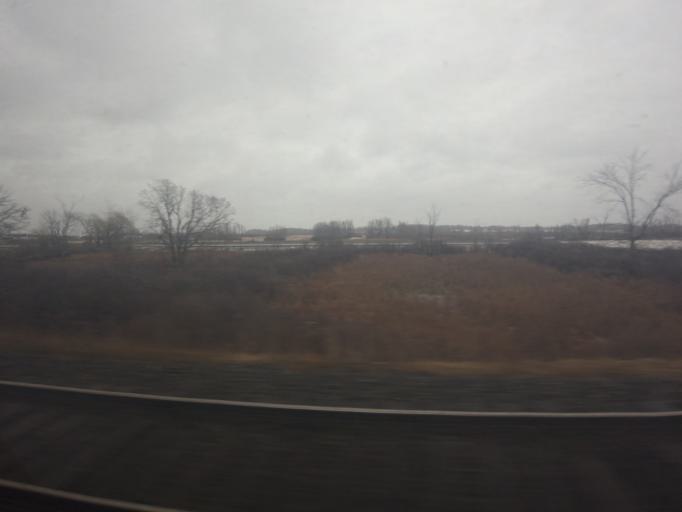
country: CA
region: Ontario
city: Kingston
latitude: 44.3231
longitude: -76.3418
